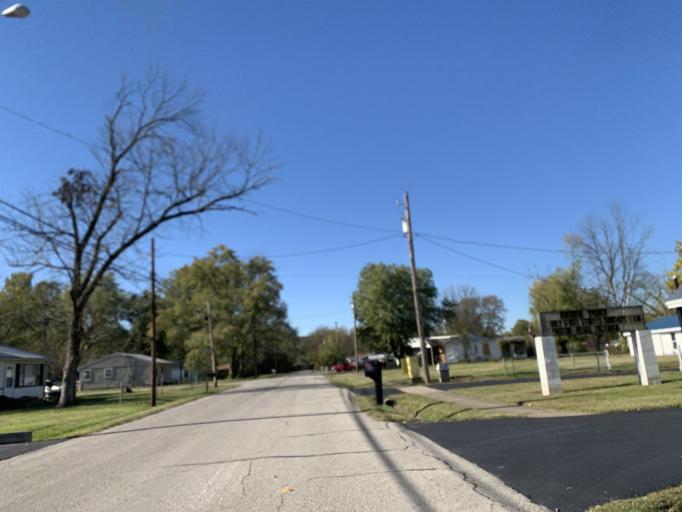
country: US
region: Kentucky
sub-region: Jefferson County
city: Saint Dennis
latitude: 38.1931
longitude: -85.8749
